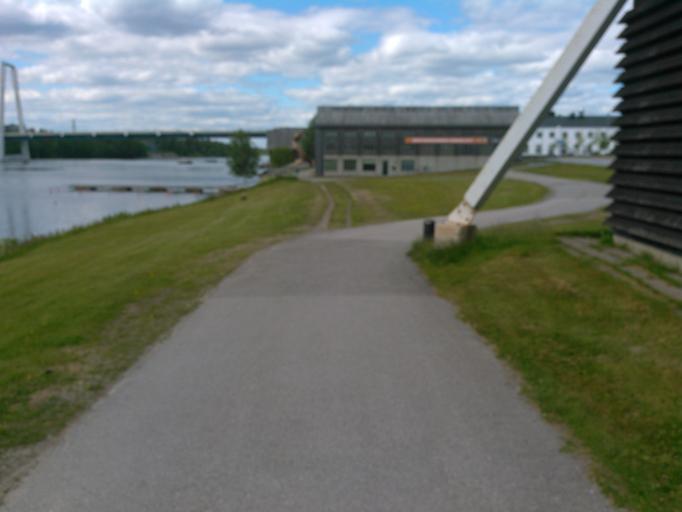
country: SE
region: Vaesterbotten
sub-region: Umea Kommun
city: Umea
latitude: 63.7982
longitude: 20.3005
